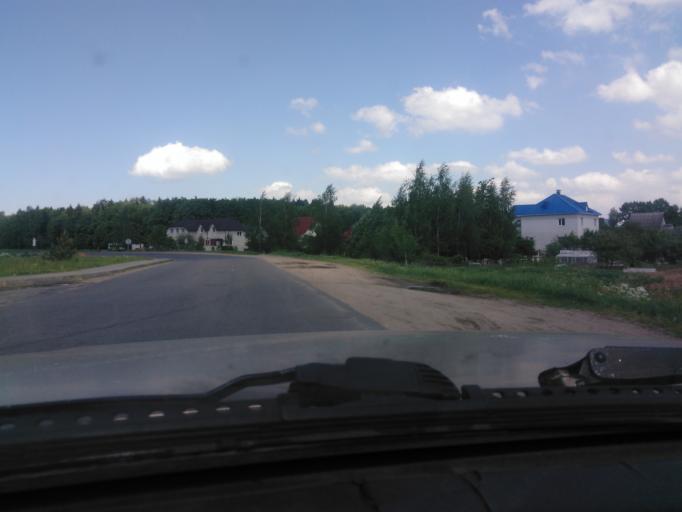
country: BY
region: Mogilev
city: Palykavichy Pyershyya
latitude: 53.9521
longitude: 30.3721
